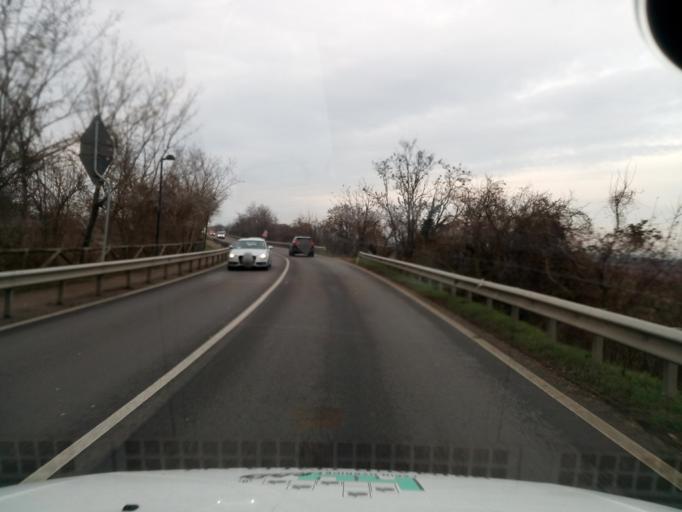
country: IT
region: Veneto
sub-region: Provincia di Vicenza
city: Montebello Vicentino
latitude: 45.4591
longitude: 11.3898
